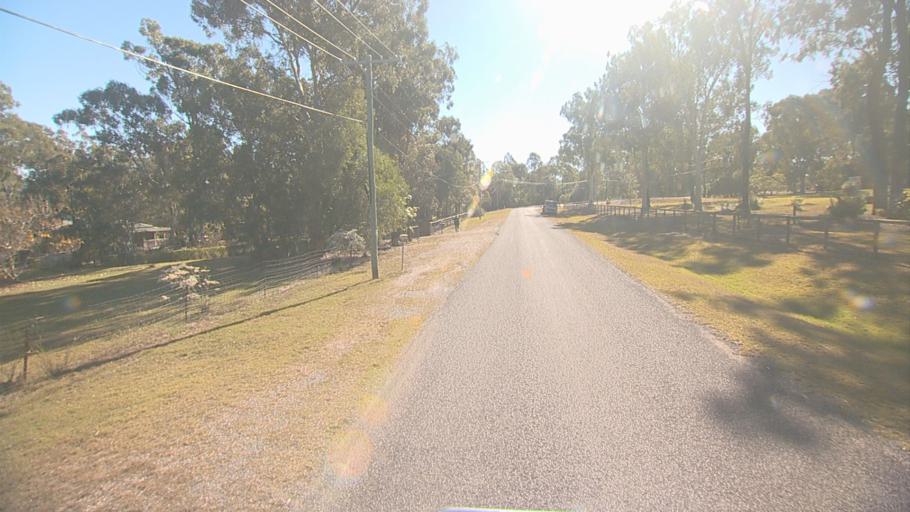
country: AU
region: Queensland
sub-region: Logan
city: Chambers Flat
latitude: -27.7914
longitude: 153.1289
